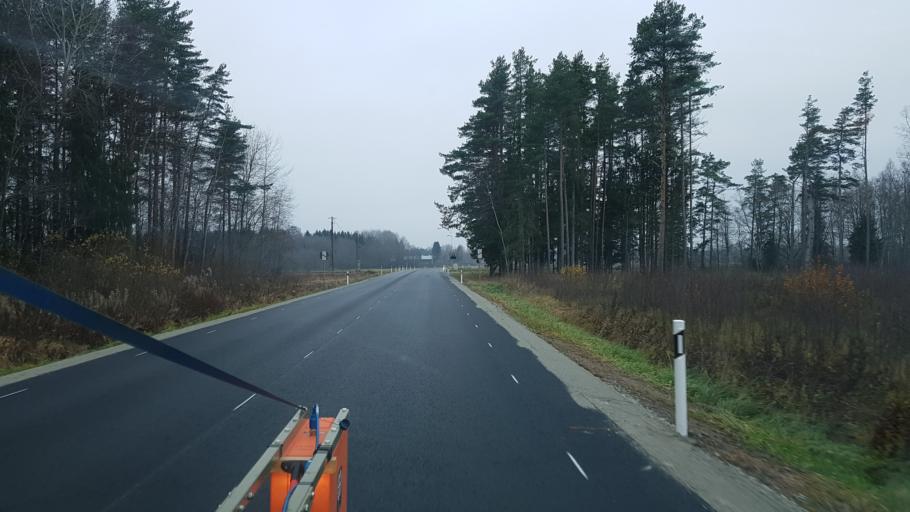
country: EE
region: Raplamaa
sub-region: Kehtna vald
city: Kehtna
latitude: 58.8533
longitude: 25.0140
